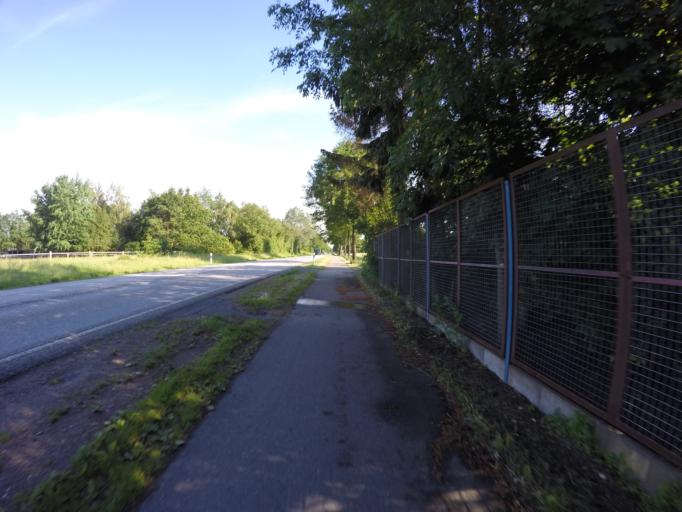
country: DE
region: Schleswig-Holstein
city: Lentfohrden
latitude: 53.8633
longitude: 9.8885
